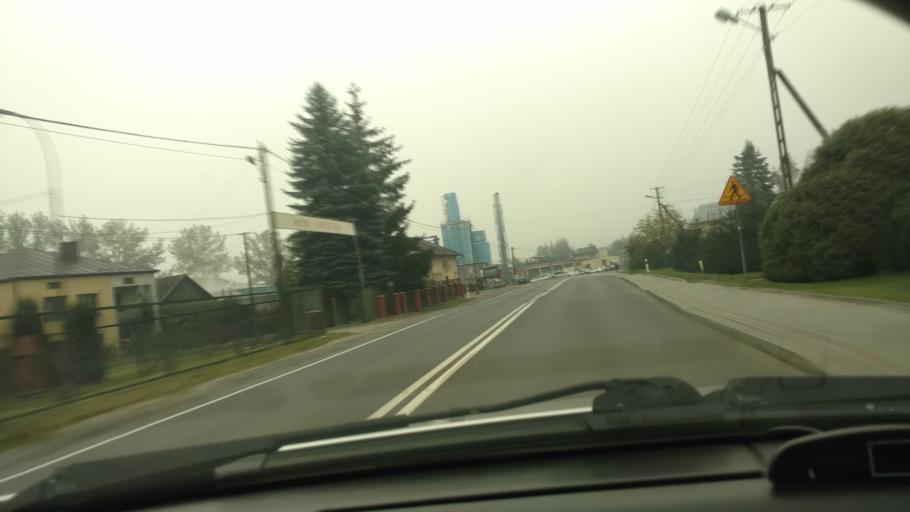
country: PL
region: Subcarpathian Voivodeship
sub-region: Powiat strzyzowski
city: Frysztak
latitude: 49.8306
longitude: 21.6169
